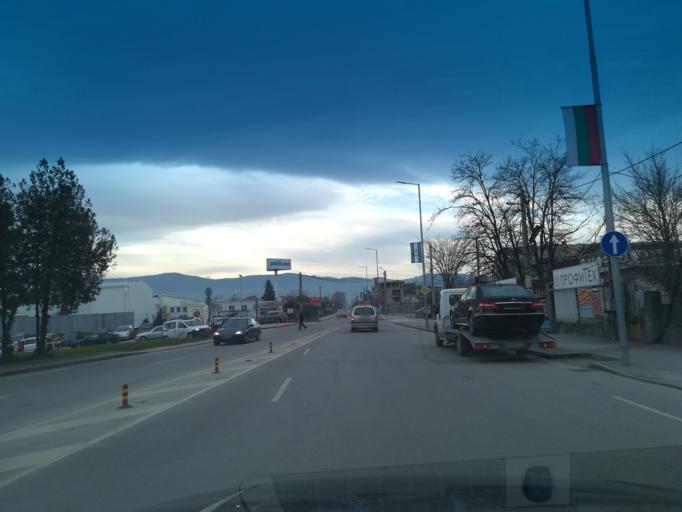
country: BG
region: Plovdiv
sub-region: Obshtina Plovdiv
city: Plovdiv
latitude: 42.1251
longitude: 24.7196
